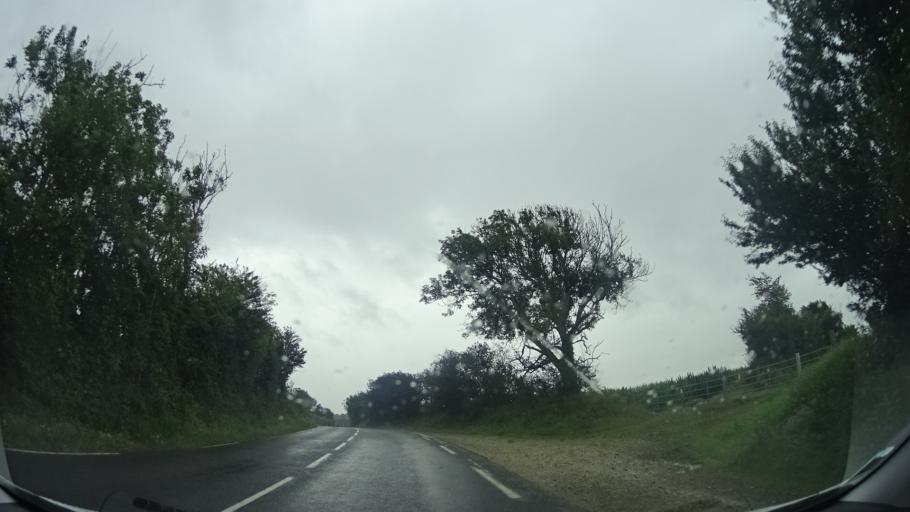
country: FR
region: Lower Normandy
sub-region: Departement de la Manche
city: Beaumont-Hague
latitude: 49.6060
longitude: -1.7875
